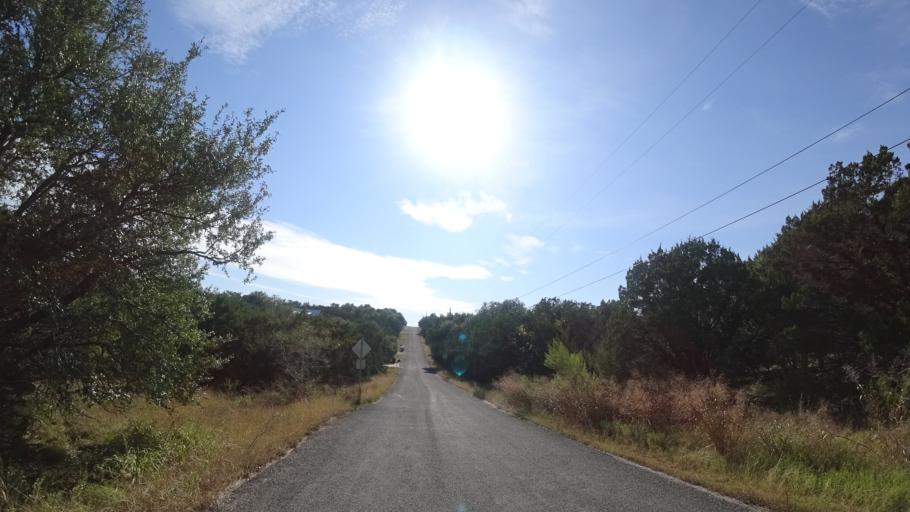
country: US
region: Texas
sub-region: Travis County
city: Barton Creek
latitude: 30.2265
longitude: -97.9071
